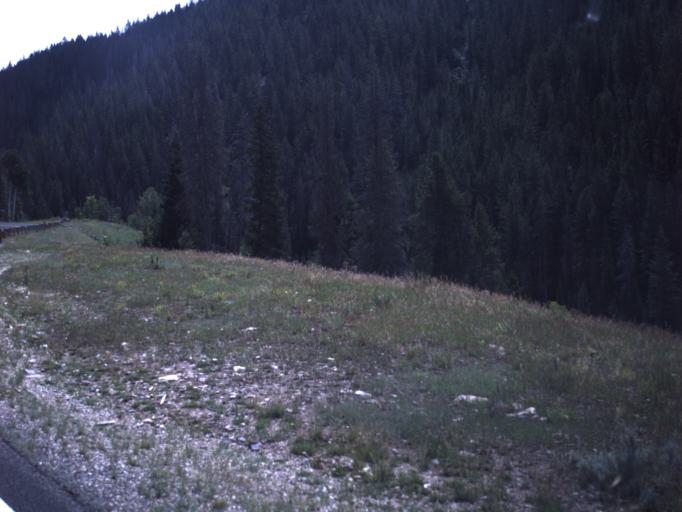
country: US
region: Utah
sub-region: Summit County
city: Francis
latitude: 40.5151
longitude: -111.0655
